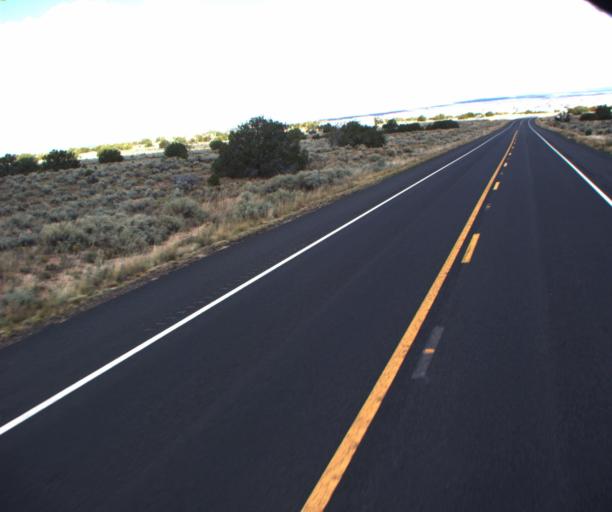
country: US
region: Arizona
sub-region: Apache County
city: Houck
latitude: 35.1772
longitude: -109.3379
